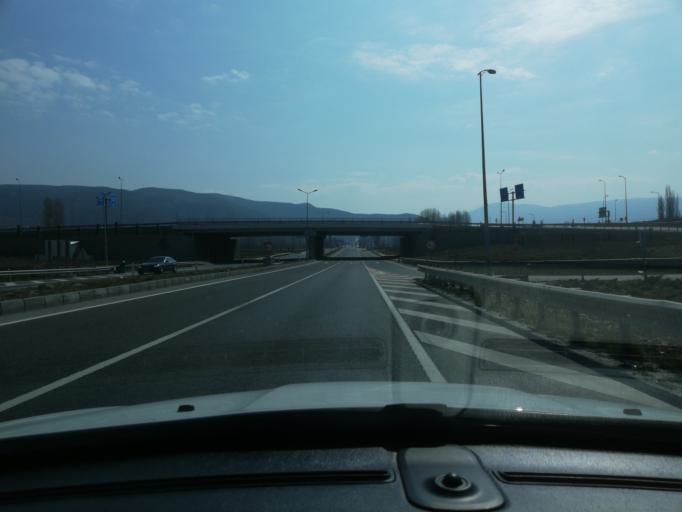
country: TR
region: Cankiri
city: Ilgaz
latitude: 40.9054
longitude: 33.6490
